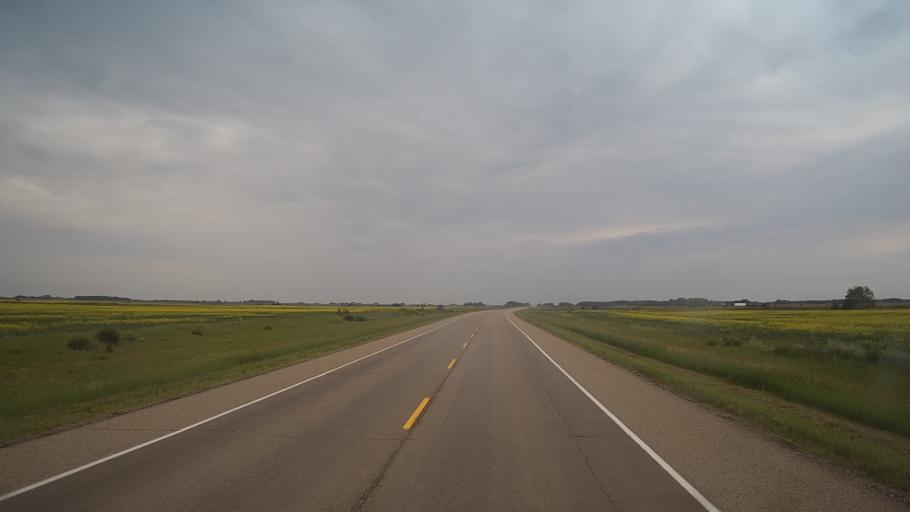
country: CA
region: Saskatchewan
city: Langham
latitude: 52.1278
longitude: -107.2463
